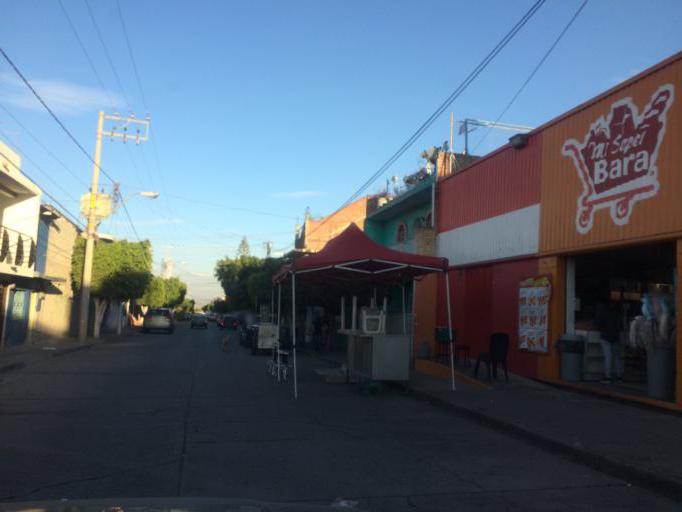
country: MX
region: Guanajuato
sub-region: Leon
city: La Ermita
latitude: 21.1370
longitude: -101.7106
